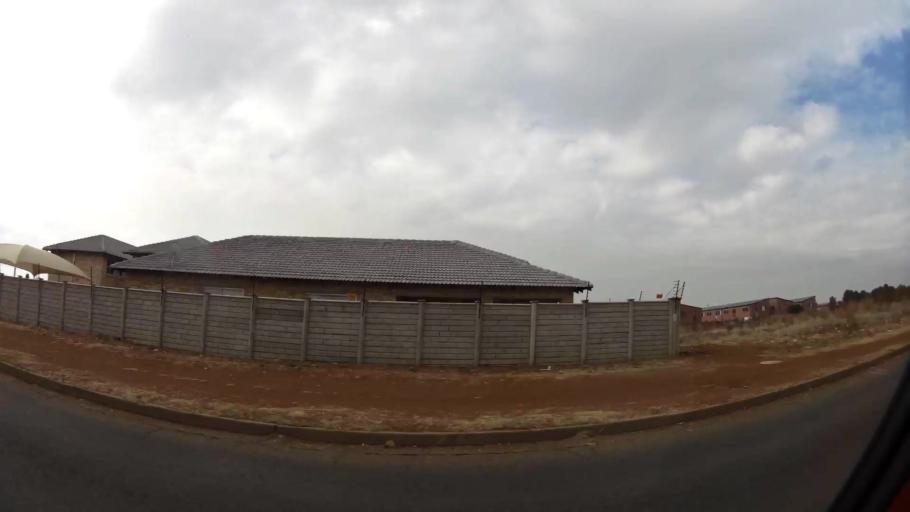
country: ZA
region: Gauteng
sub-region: Sedibeng District Municipality
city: Vanderbijlpark
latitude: -26.7188
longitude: 27.8632
